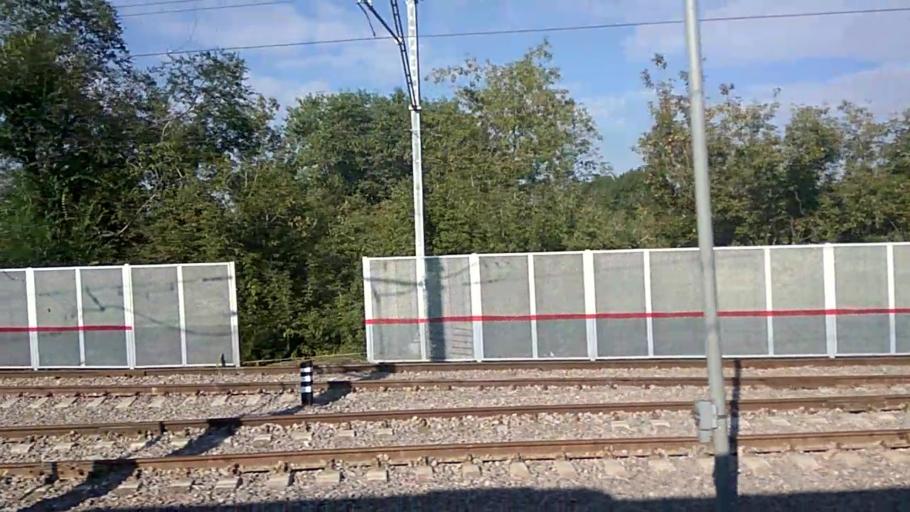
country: RU
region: Moscow
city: Ryazanskiy
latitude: 55.7352
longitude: 37.7302
